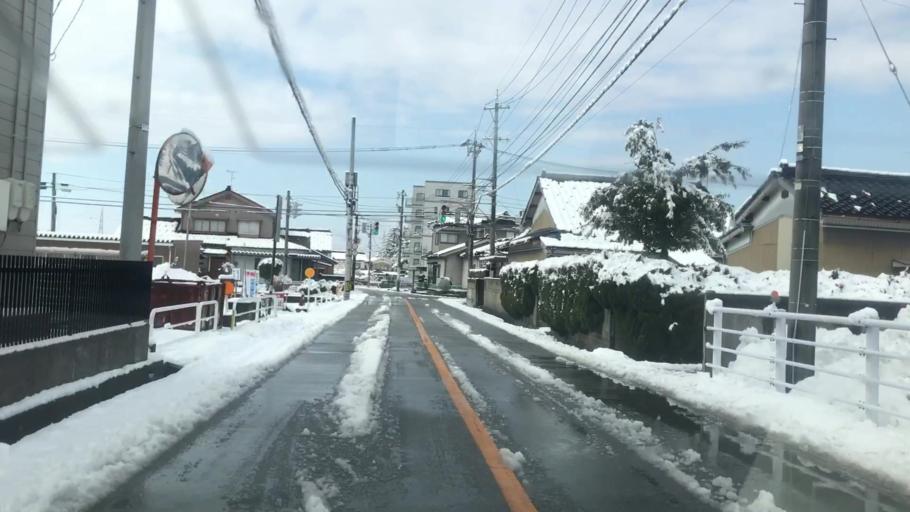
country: JP
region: Toyama
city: Toyama-shi
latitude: 36.6307
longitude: 137.2316
